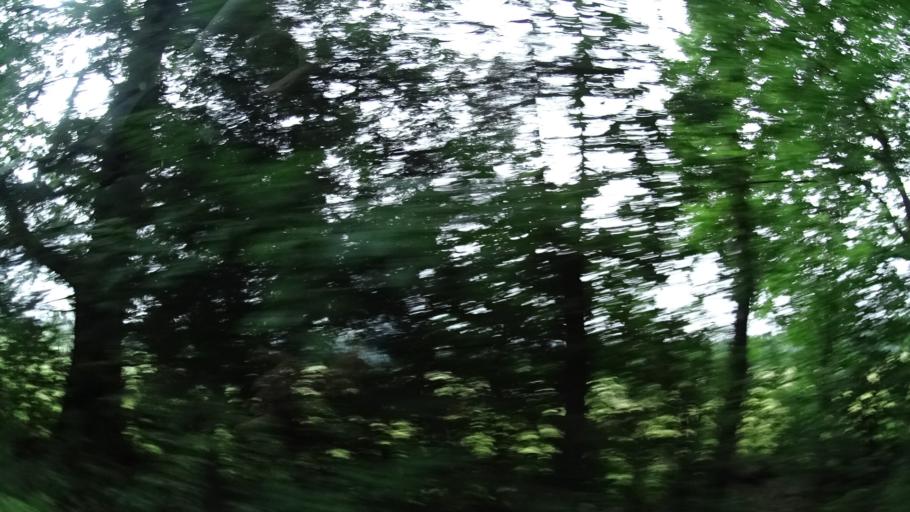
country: BE
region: Wallonia
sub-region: Province du Luxembourg
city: Habay-la-Vieille
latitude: 49.7448
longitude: 5.6123
